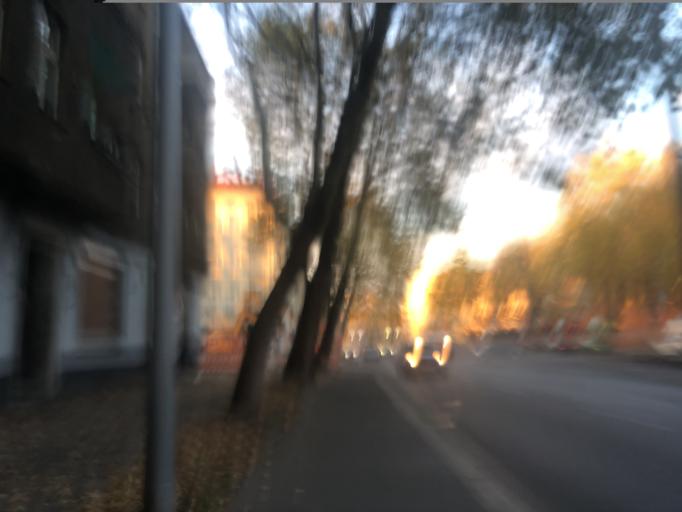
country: DE
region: Berlin
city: Weissensee
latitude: 52.5494
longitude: 13.4667
